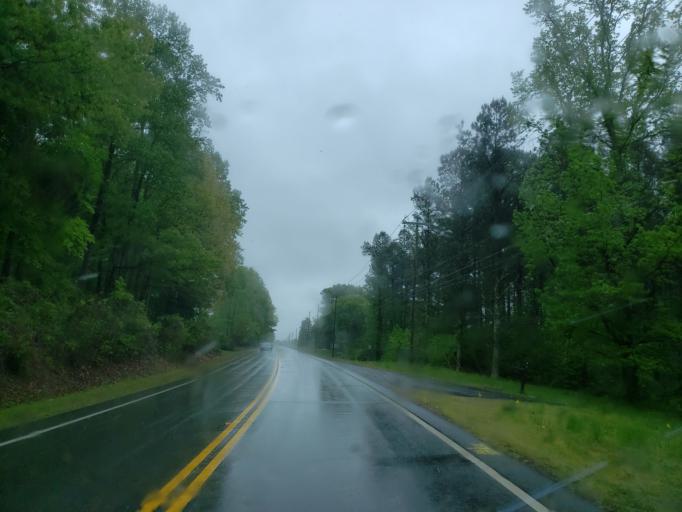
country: US
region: Georgia
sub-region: Carroll County
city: Villa Rica
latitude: 33.7345
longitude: -84.9704
